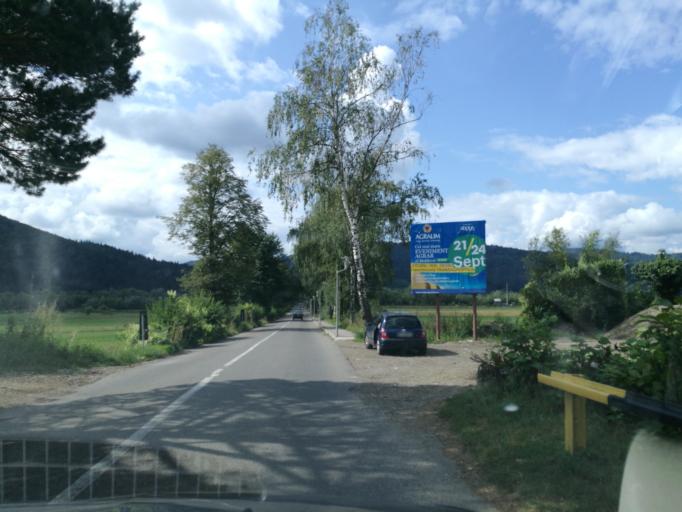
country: RO
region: Suceava
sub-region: Oras Gura Humorului
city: Gura Humorului
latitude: 47.5475
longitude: 25.8726
